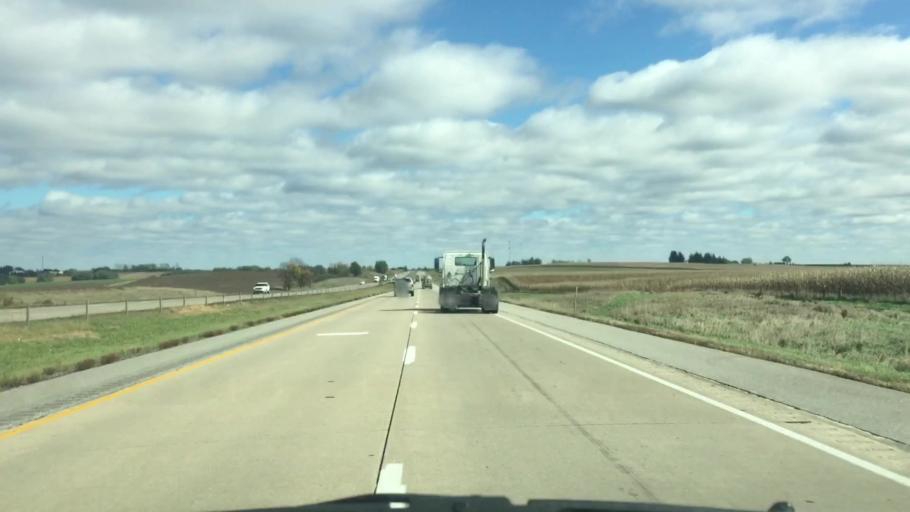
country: US
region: Iowa
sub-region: Poweshiek County
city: Brooklyn
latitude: 41.6941
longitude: -92.4932
